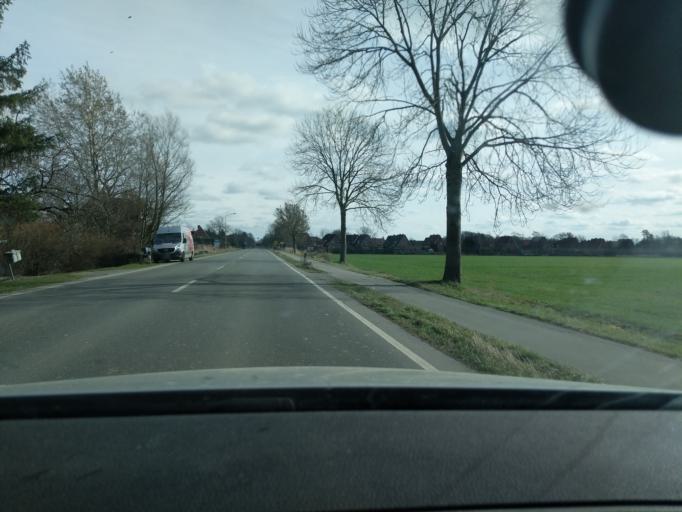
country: DE
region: Lower Saxony
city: Drochtersen
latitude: 53.7017
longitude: 9.4068
